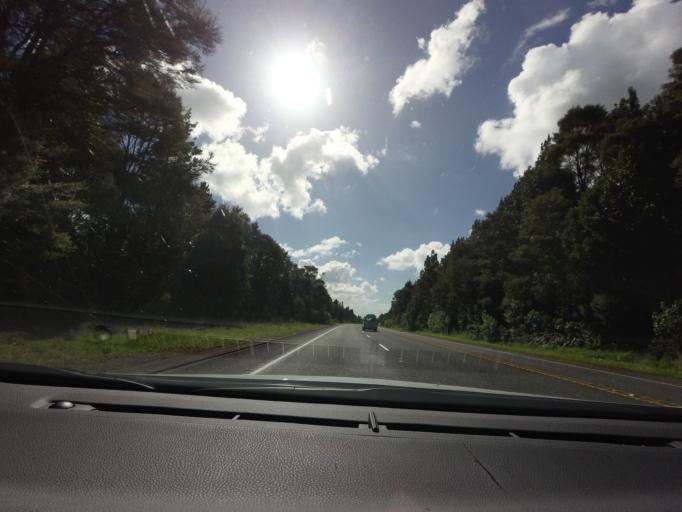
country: NZ
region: Waikato
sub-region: South Waikato District
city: Tokoroa
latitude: -38.0178
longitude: 175.9526
